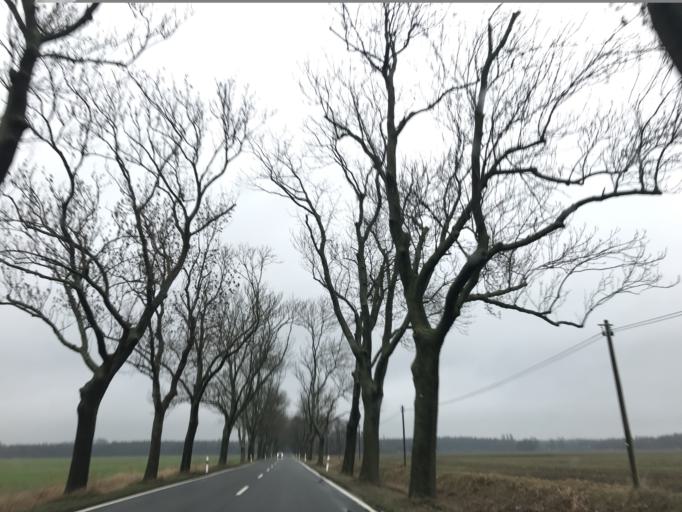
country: DE
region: Brandenburg
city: Brieselang
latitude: 52.6064
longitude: 12.9616
